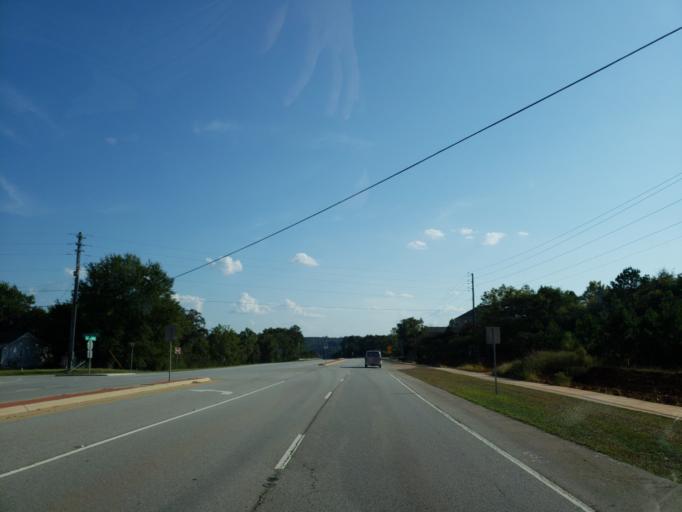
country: US
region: Georgia
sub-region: Paulding County
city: Hiram
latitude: 33.8911
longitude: -84.7799
